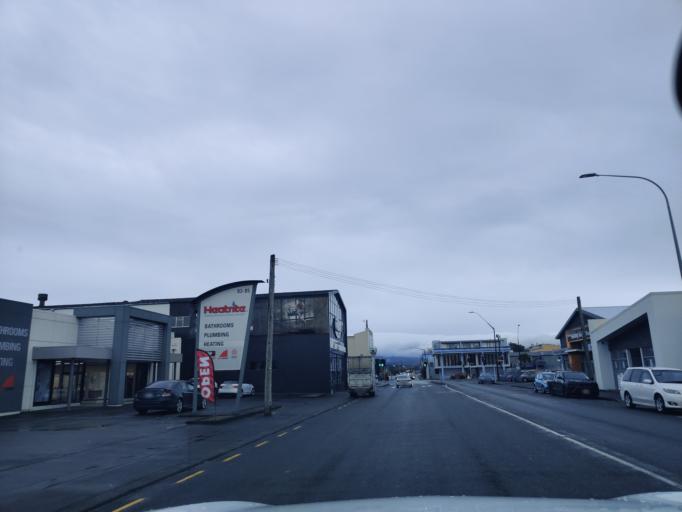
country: NZ
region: Manawatu-Wanganui
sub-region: Palmerston North City
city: Palmerston North
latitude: -40.3558
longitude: 175.6045
